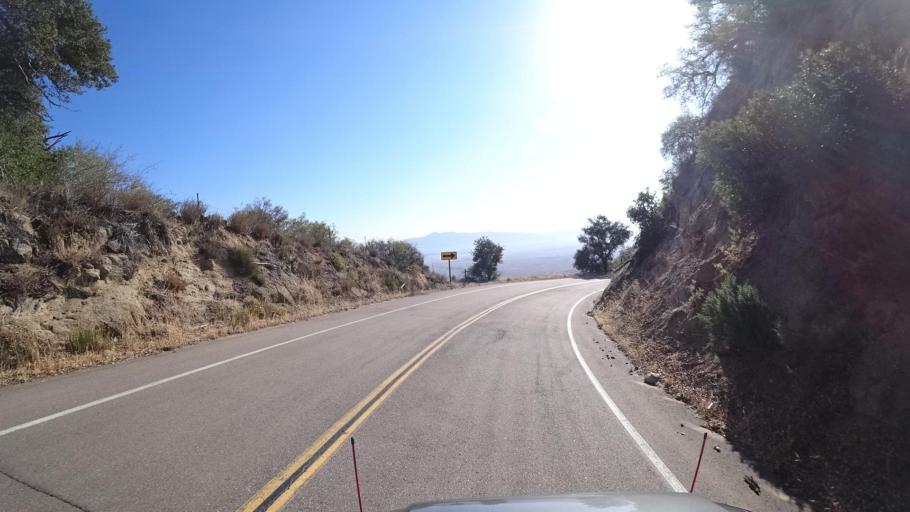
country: US
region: California
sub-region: Riverside County
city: Aguanga
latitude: 33.2665
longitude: -116.7697
